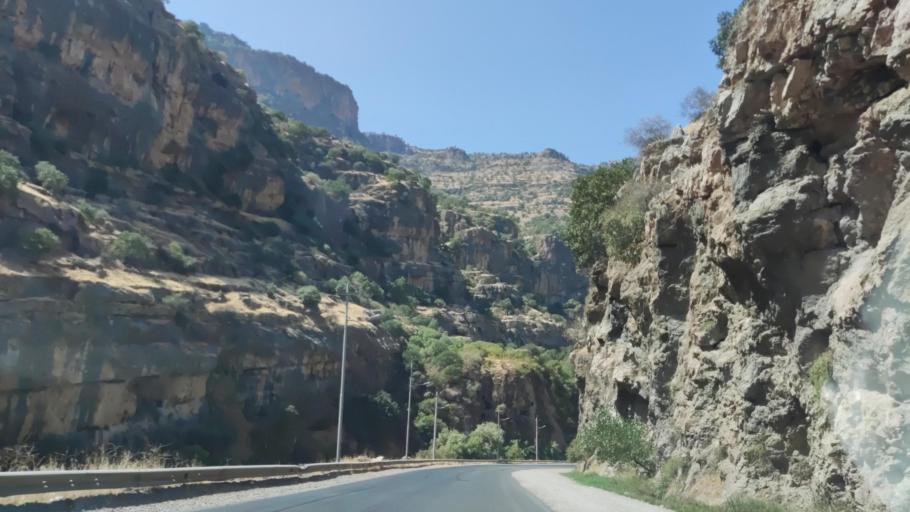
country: IQ
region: Arbil
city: Ruwandiz
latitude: 36.6275
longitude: 44.4684
